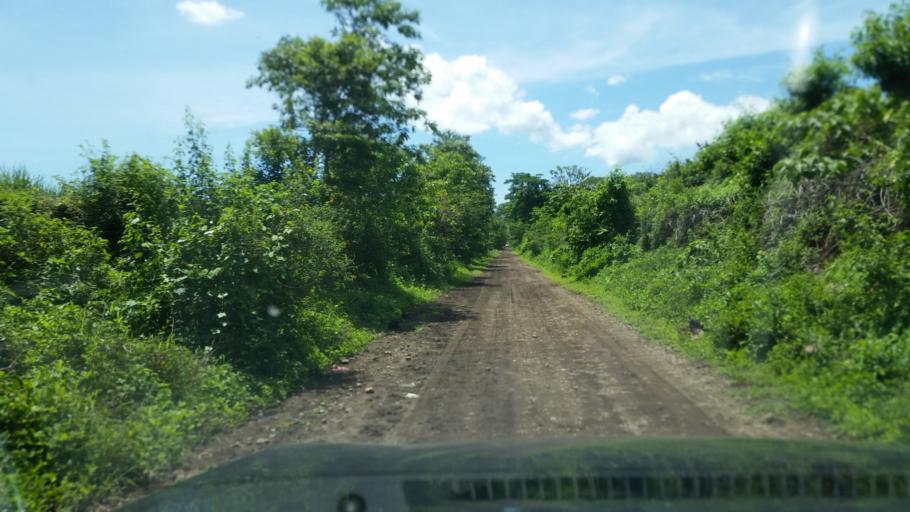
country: NI
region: Chinandega
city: Puerto Morazan
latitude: 12.7613
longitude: -87.1313
